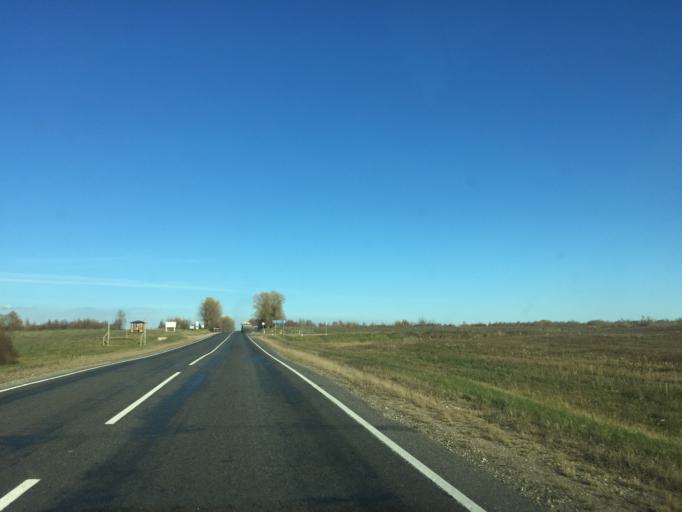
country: BY
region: Vitebsk
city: Dzisna
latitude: 55.3544
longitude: 28.3329
